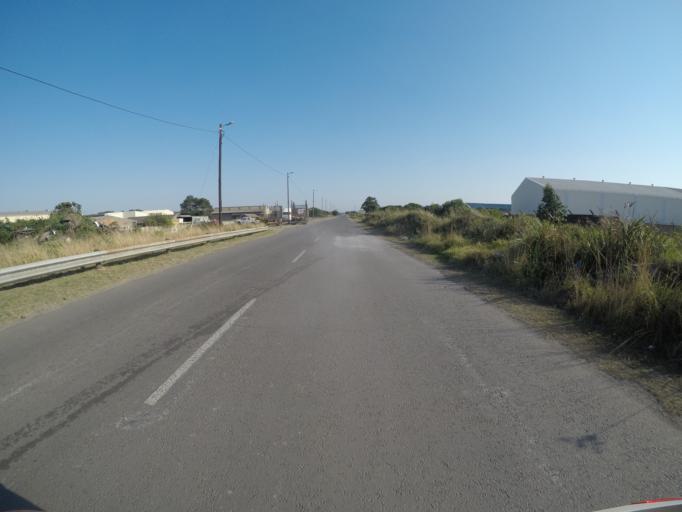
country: ZA
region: KwaZulu-Natal
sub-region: uThungulu District Municipality
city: Richards Bay
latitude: -28.7557
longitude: 32.0303
